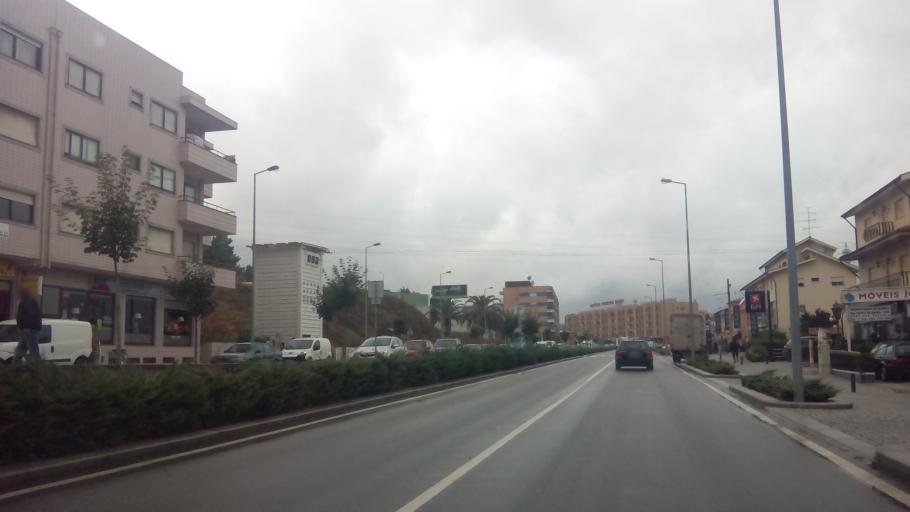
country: PT
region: Porto
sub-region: Valongo
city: Campo
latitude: 41.1837
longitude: -8.4460
